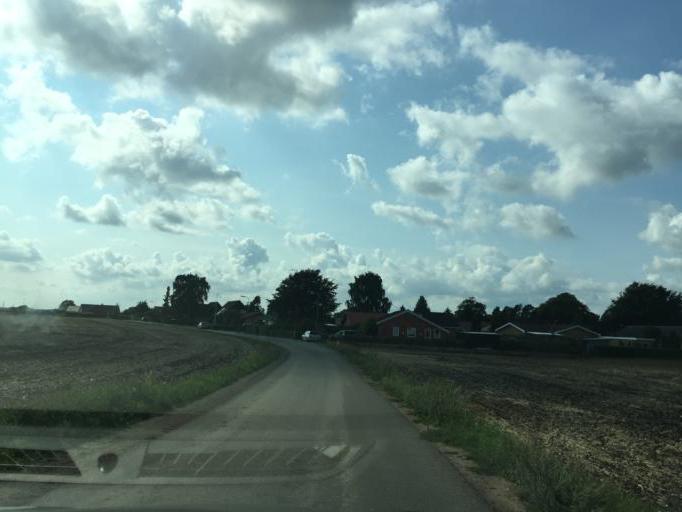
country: DK
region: South Denmark
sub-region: Odense Kommune
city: Bellinge
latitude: 55.3383
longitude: 10.3653
